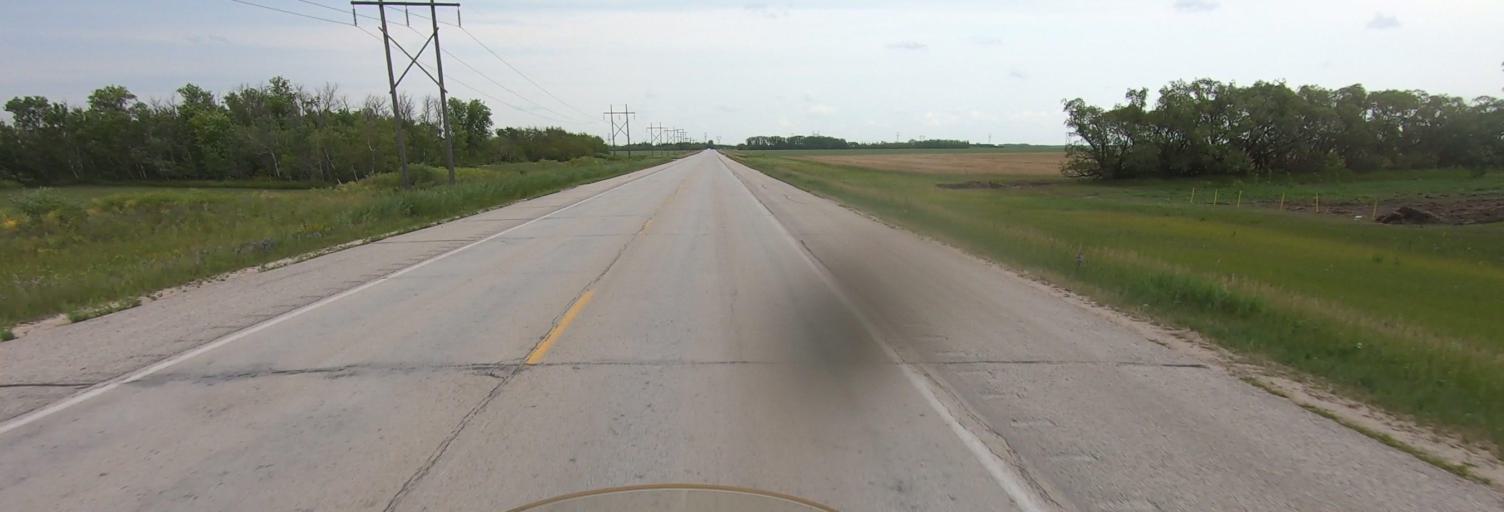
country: CA
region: Manitoba
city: Headingley
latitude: 49.7291
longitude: -97.3676
